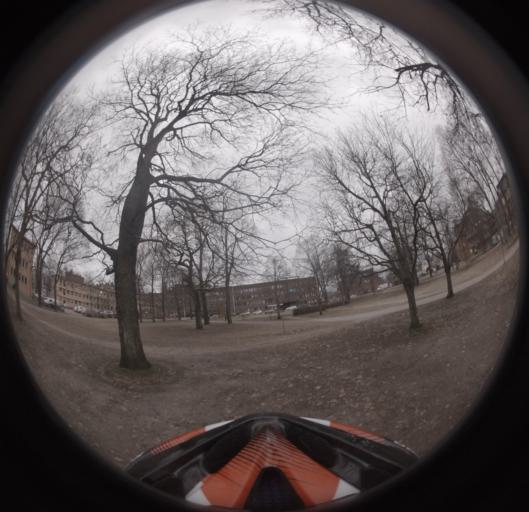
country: SE
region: Vaermland
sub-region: Karlstads Kommun
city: Karlstad
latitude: 59.3826
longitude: 13.4932
